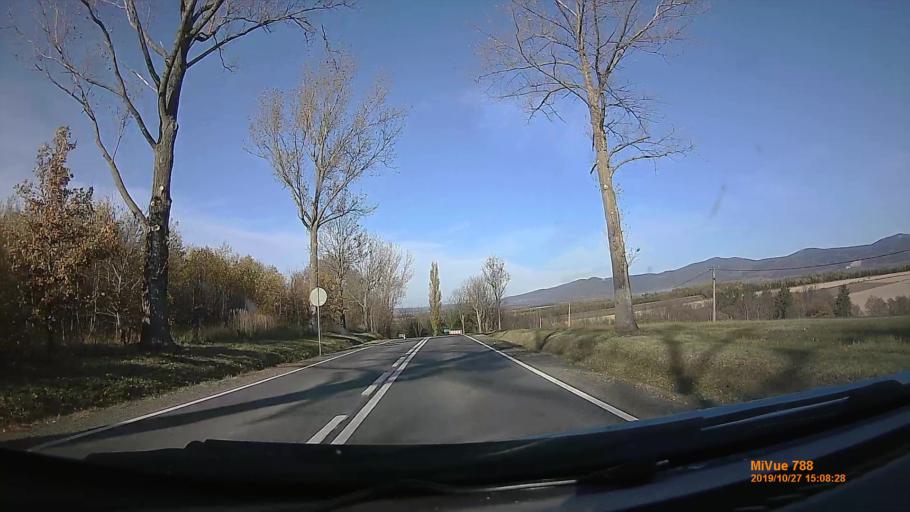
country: PL
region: Lower Silesian Voivodeship
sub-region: Powiat klodzki
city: Miedzylesie
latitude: 50.1705
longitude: 16.6691
